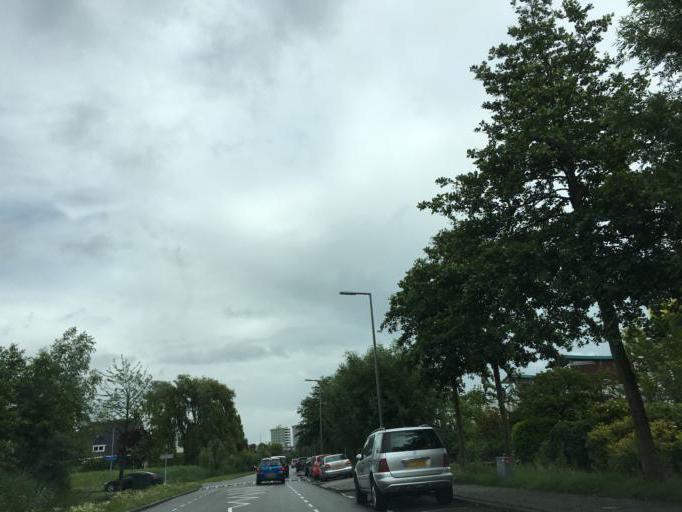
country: NL
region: South Holland
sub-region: Gemeente Rotterdam
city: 's-Gravenland
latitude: 51.9218
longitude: 4.5470
